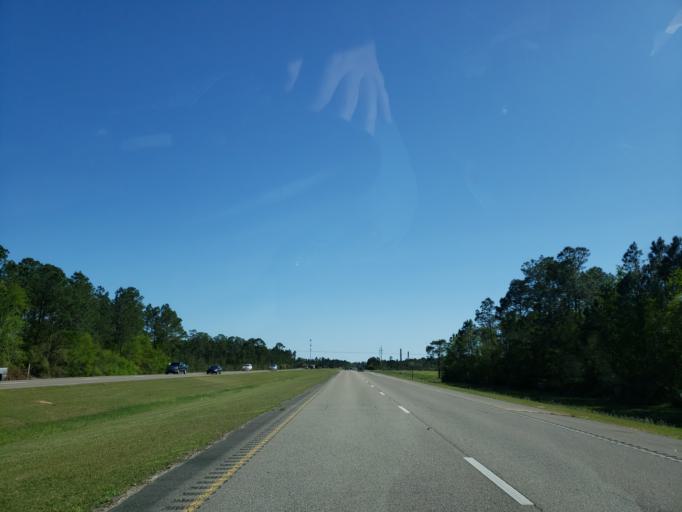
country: US
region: Mississippi
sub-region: Harrison County
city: West Gulfport
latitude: 30.4694
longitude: -89.0281
